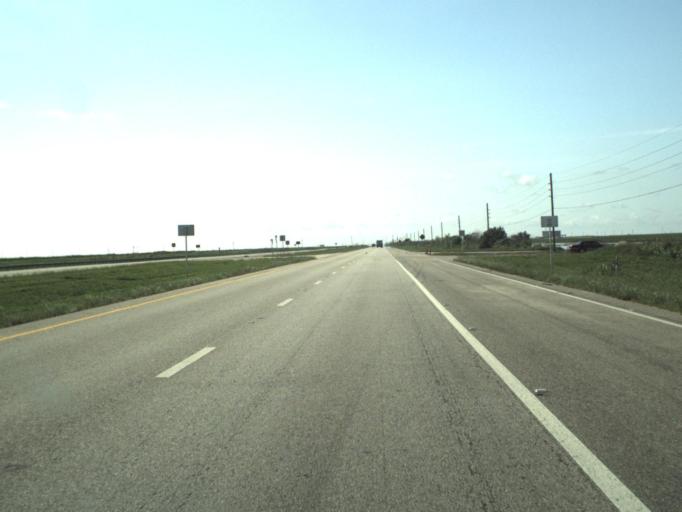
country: US
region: Florida
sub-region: Palm Beach County
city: Belle Glade Camp
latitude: 26.4155
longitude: -80.6003
